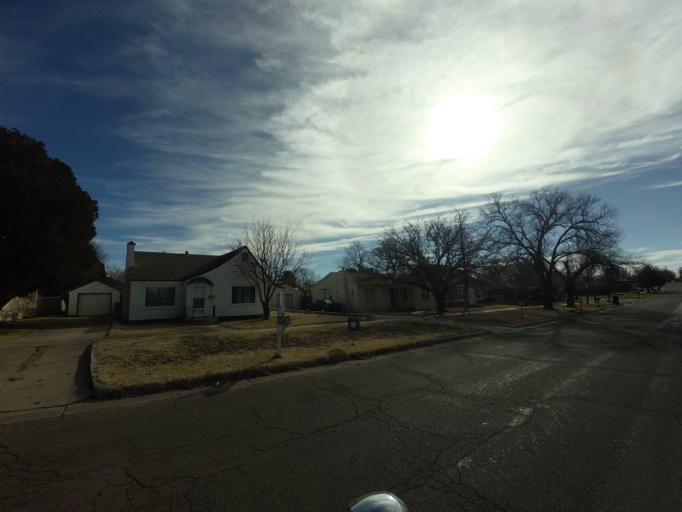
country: US
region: New Mexico
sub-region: Curry County
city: Clovis
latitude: 34.4168
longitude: -103.2029
